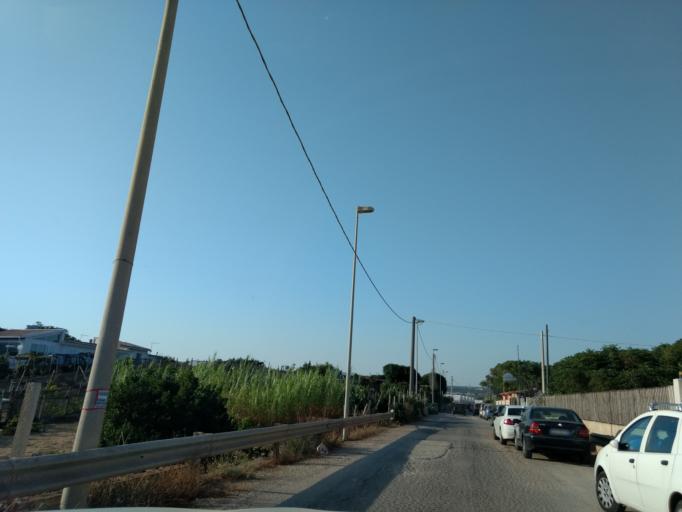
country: IT
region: Sicily
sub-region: Ragusa
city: Donnalucata
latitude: 36.7473
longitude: 14.6629
